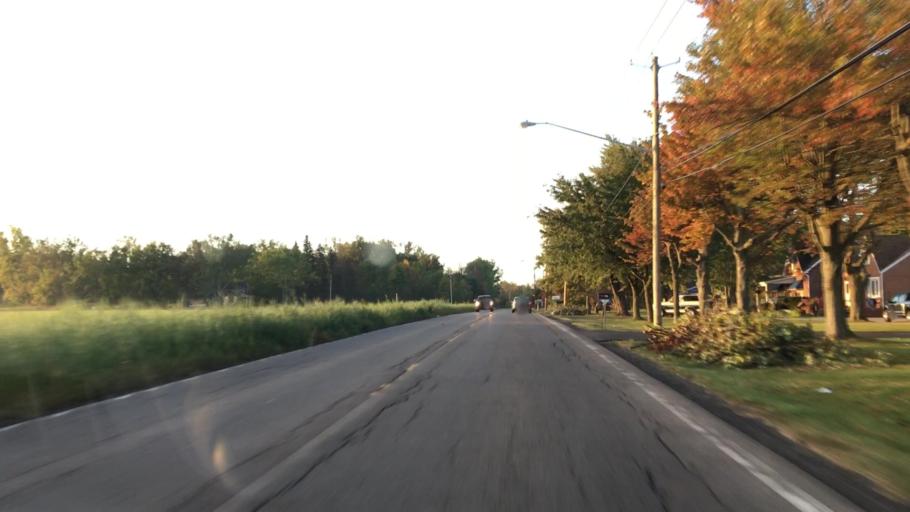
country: US
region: New York
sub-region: Erie County
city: Lancaster
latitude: 42.8626
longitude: -78.6762
